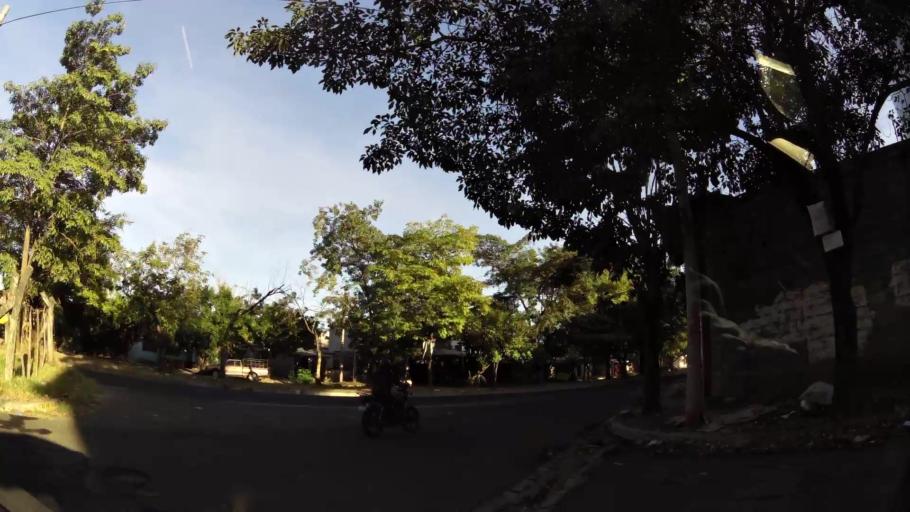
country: SV
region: San Miguel
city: San Miguel
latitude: 13.4589
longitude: -88.1649
